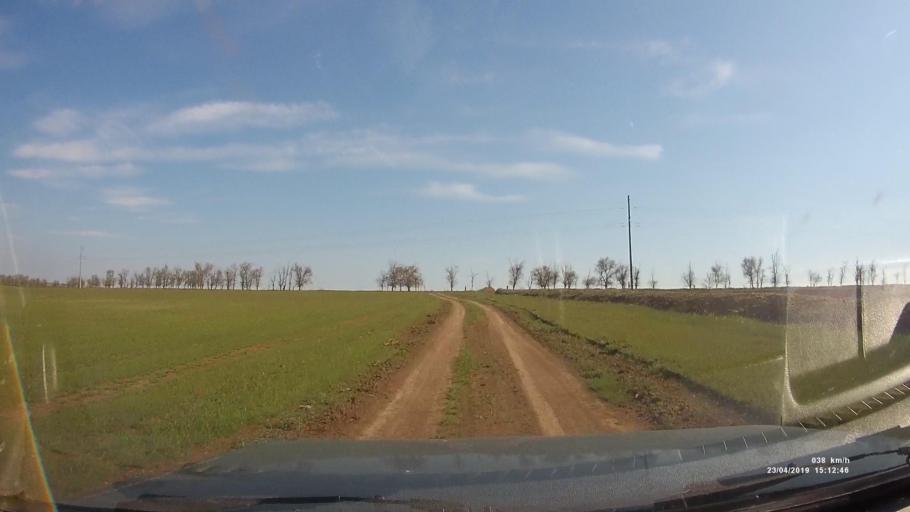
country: RU
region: Rostov
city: Remontnoye
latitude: 46.5419
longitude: 42.9512
